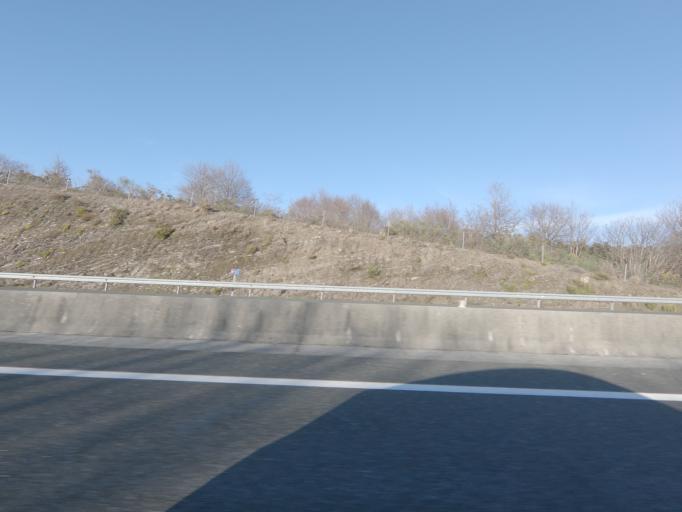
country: ES
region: Galicia
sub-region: Provincia de Pontevedra
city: Dozon
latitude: 42.5865
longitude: -8.0742
